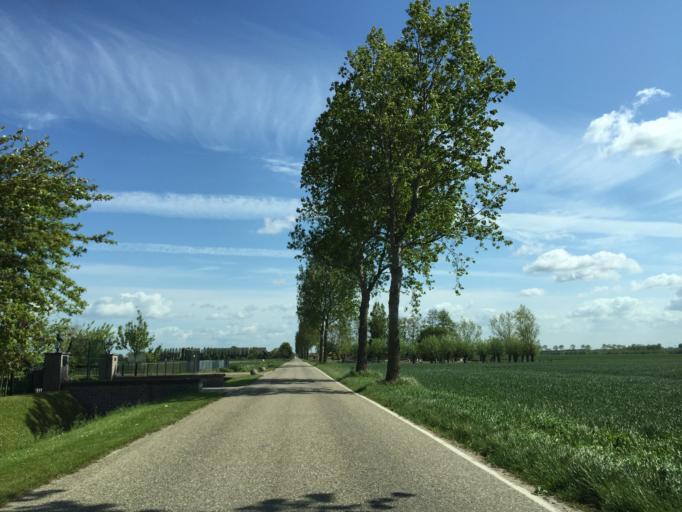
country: NL
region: North Holland
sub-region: Gemeente Haarlemmermeer
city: Hoofddorp
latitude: 52.3519
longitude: 4.7212
